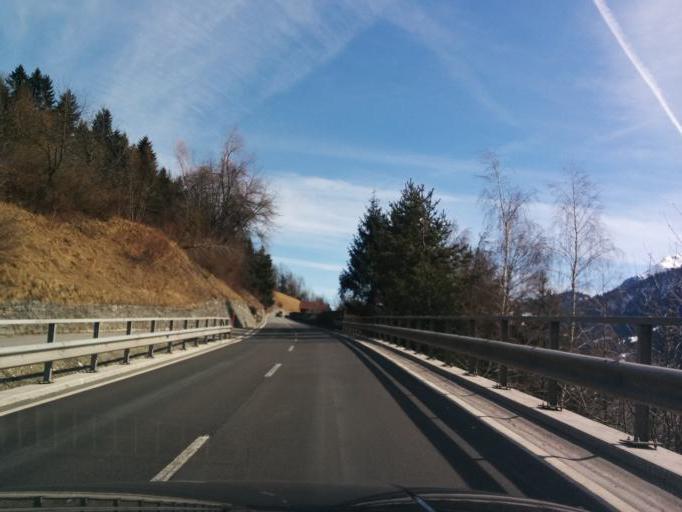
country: CH
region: Grisons
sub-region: Surselva District
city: Laax
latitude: 46.7897
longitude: 9.2320
